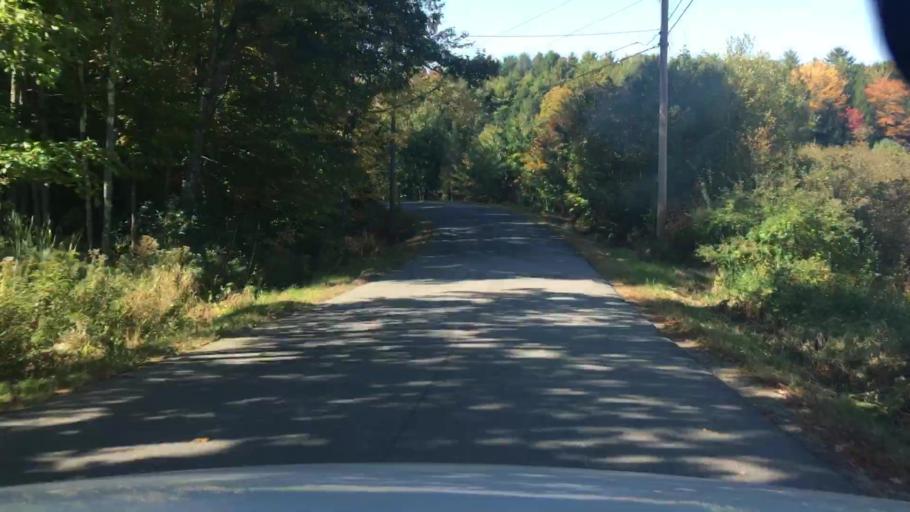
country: US
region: Maine
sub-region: Androscoggin County
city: Lisbon Falls
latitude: 44.0190
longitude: -69.9870
